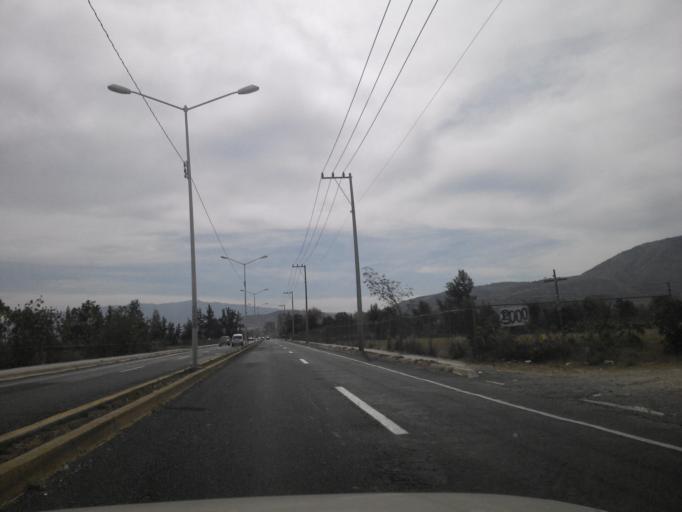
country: MX
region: Jalisco
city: San Sebastian el Grande
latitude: 20.5227
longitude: -103.4091
